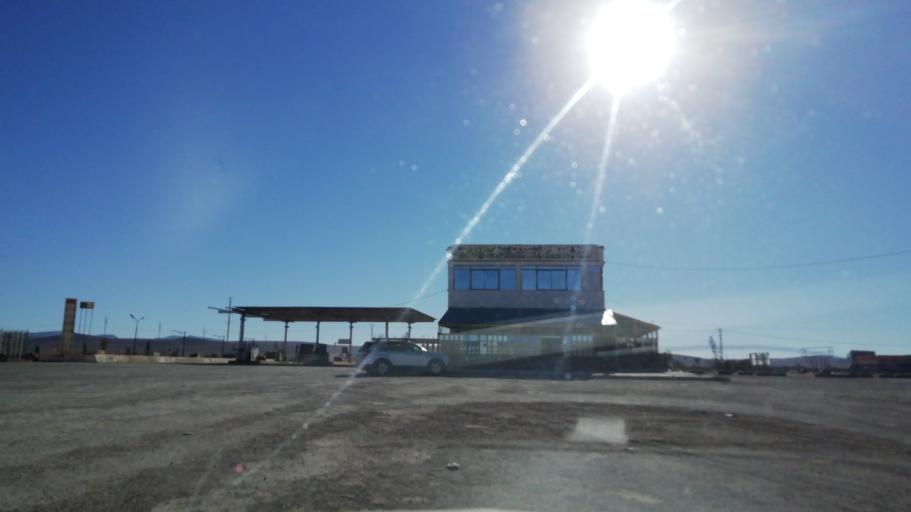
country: DZ
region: El Bayadh
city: El Bayadh
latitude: 33.6557
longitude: 0.9061
